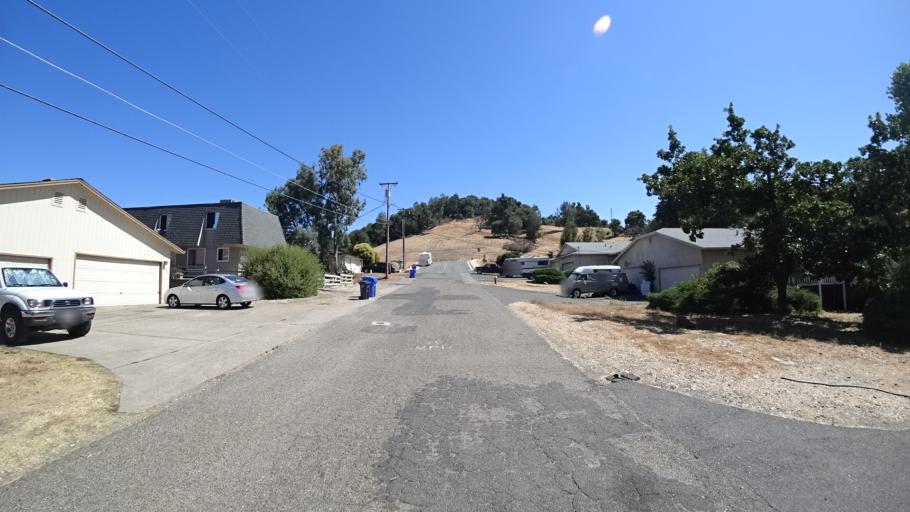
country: US
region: California
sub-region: Calaveras County
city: San Andreas
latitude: 38.1979
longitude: -120.6746
